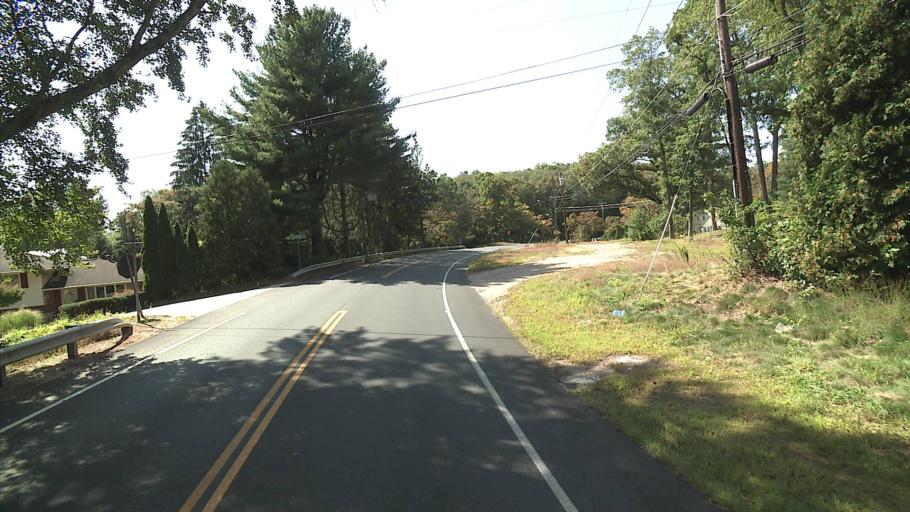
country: US
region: Connecticut
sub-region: Tolland County
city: Coventry Lake
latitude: 41.7165
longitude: -72.3254
